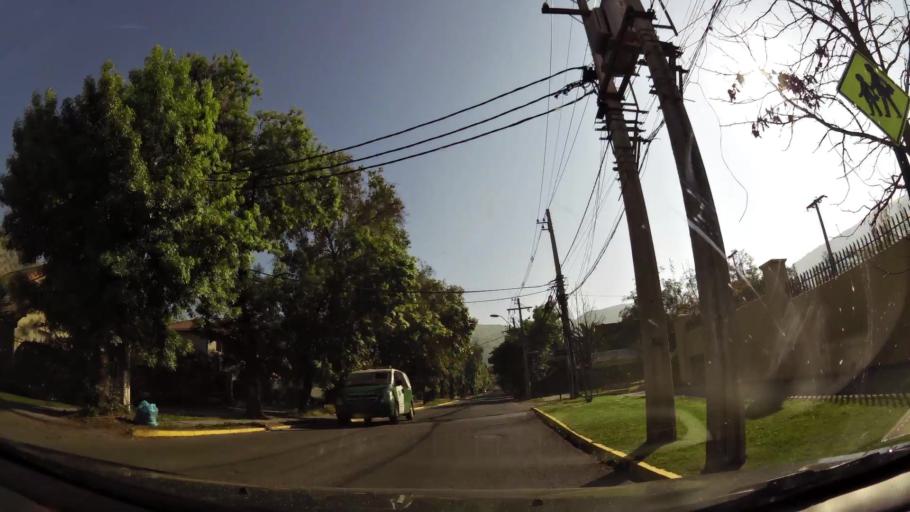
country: CL
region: Santiago Metropolitan
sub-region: Provincia de Chacabuco
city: Chicureo Abajo
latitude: -33.3436
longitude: -70.6694
